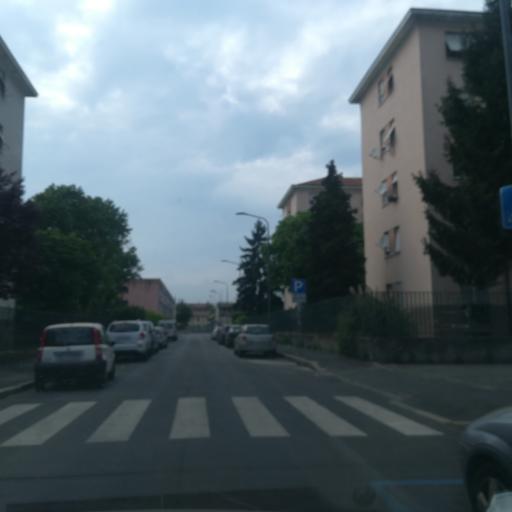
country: IT
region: Lombardy
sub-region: Citta metropolitana di Milano
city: Bresso
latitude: 45.5056
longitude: 9.1924
